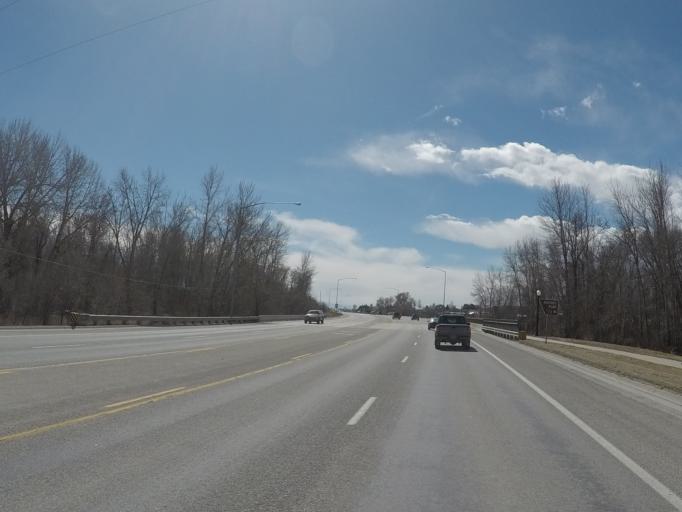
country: US
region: Montana
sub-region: Missoula County
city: Lolo
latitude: 46.7505
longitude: -114.0830
